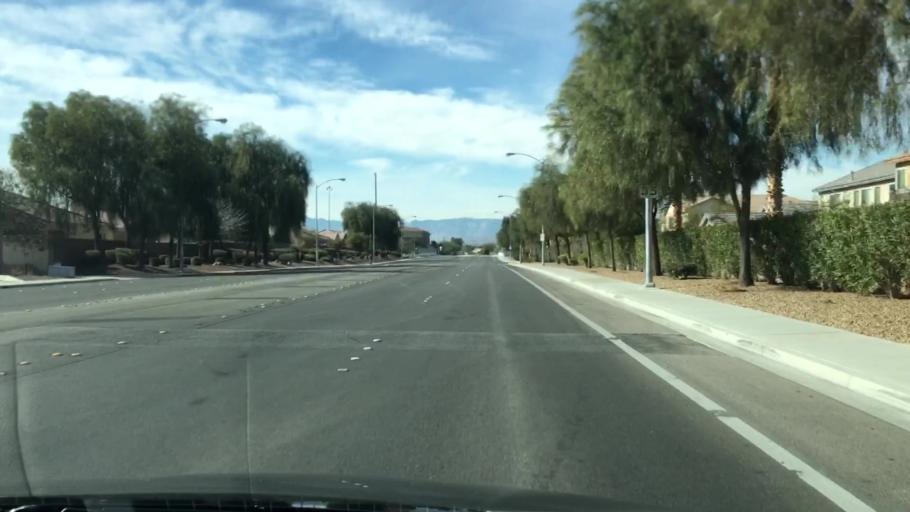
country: US
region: Nevada
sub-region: Clark County
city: Whitney
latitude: 36.0353
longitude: -115.1297
